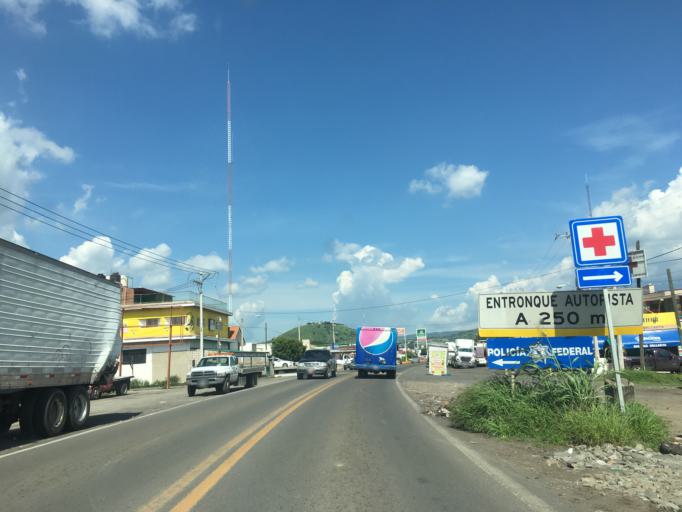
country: MX
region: Nayarit
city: Ixtlan del Rio
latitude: 21.0377
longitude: -104.3806
